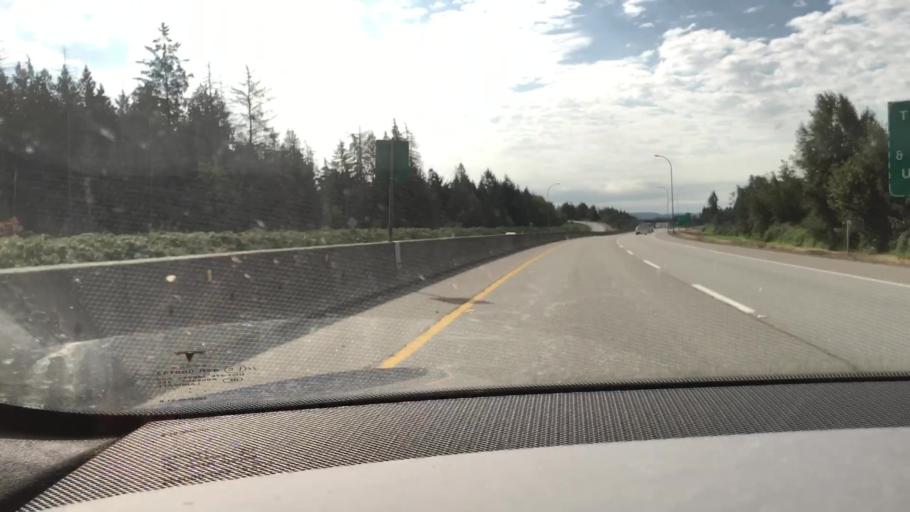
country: CA
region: British Columbia
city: Delta
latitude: 49.1090
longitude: -122.9046
